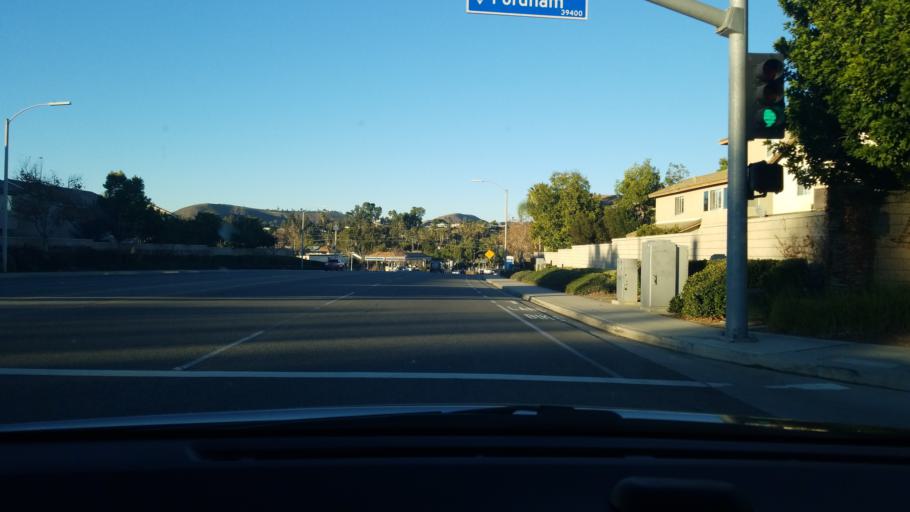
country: US
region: California
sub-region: Riverside County
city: Murrieta Hot Springs
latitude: 33.5537
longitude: -117.1577
